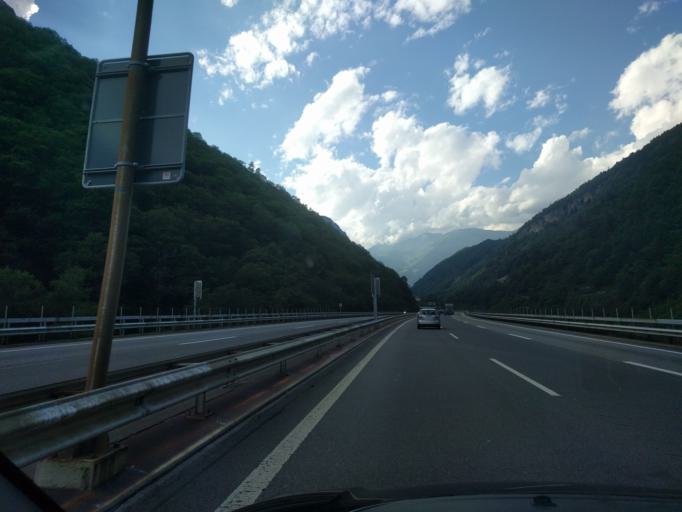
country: CH
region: Ticino
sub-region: Blenio District
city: Cancori
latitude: 46.4284
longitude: 8.8539
